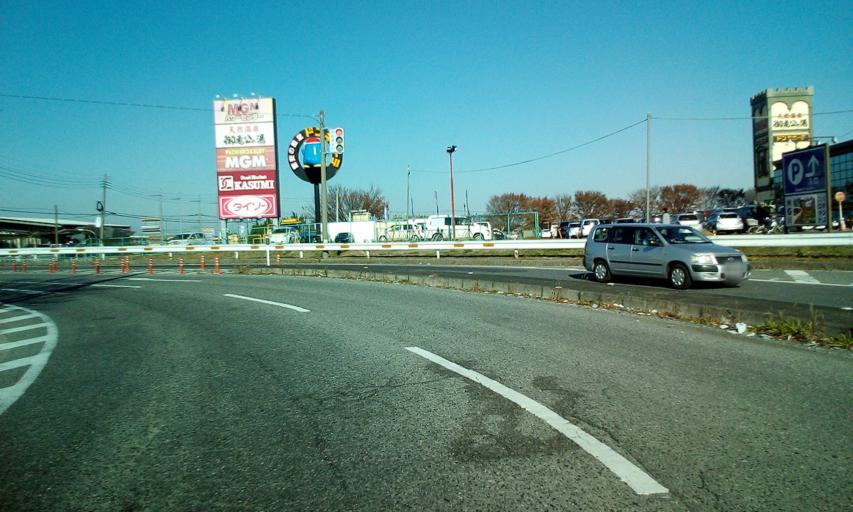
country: JP
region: Ibaraki
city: Sakai
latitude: 36.1019
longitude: 139.7959
